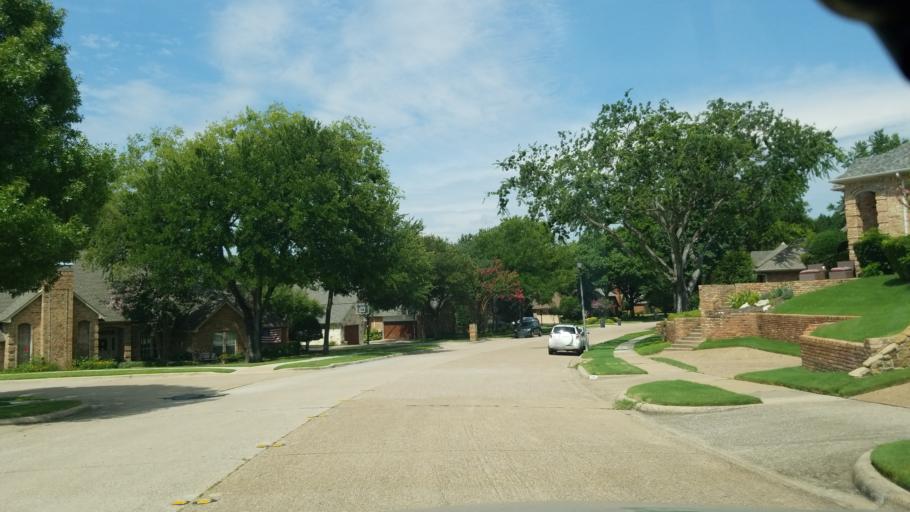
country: US
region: Texas
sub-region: Dallas County
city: Coppell
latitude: 32.9587
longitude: -96.9697
